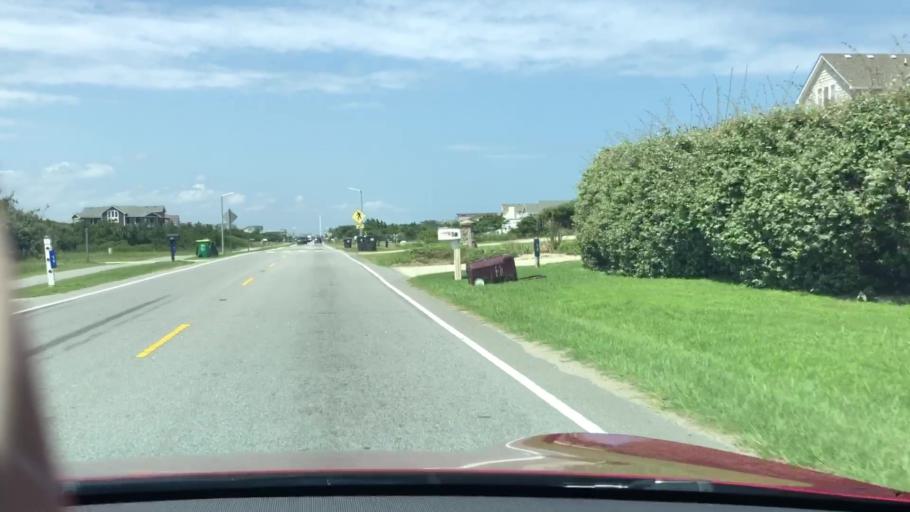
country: US
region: North Carolina
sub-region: Dare County
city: Southern Shores
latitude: 36.1087
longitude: -75.7176
